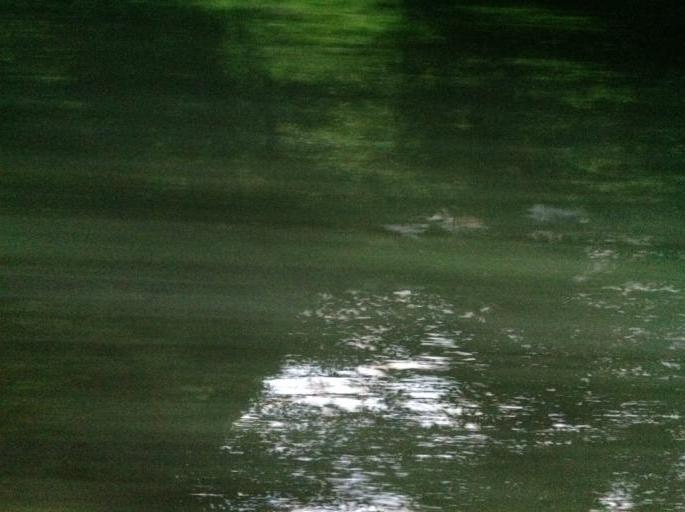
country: AT
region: Salzburg
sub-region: Salzburg Stadt
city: Salzburg
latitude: 47.8177
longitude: 13.0535
